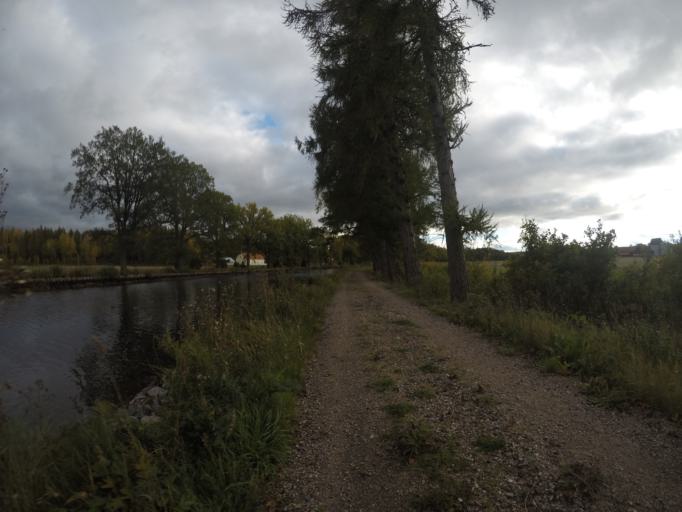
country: SE
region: Vaestmanland
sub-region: Arboga Kommun
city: Tyringe
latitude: 59.3900
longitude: 15.9391
